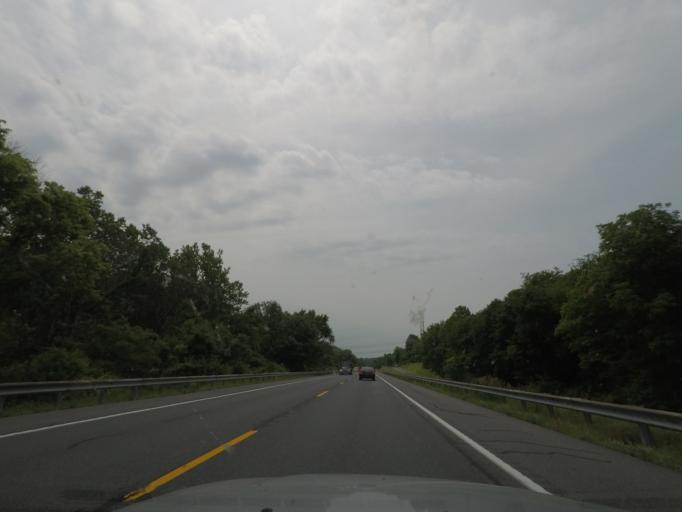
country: US
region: Maryland
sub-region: Frederick County
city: Point of Rocks
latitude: 39.3039
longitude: -77.5186
